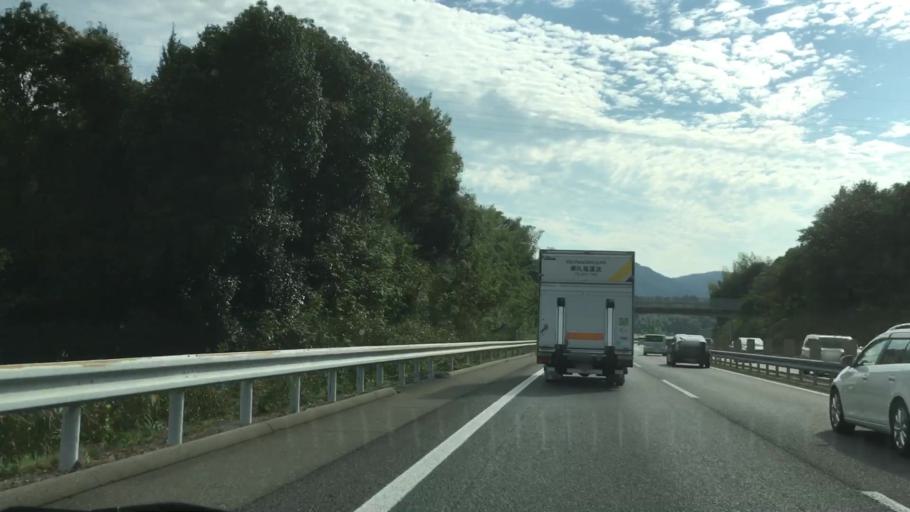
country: JP
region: Yamaguchi
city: Yanai
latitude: 34.0916
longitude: 132.0956
